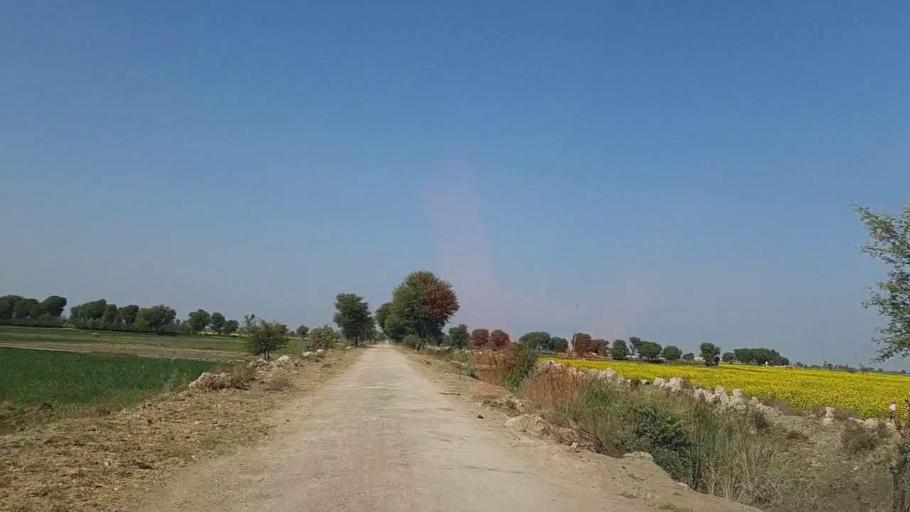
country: PK
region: Sindh
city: Sanghar
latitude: 26.0137
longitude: 69.0523
